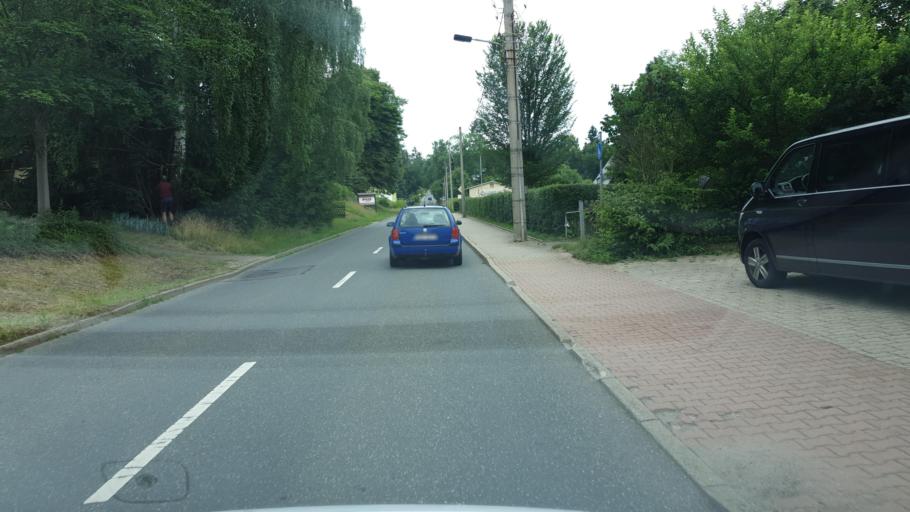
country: DE
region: Saxony
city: Grunhain
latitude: 50.5818
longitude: 12.7945
